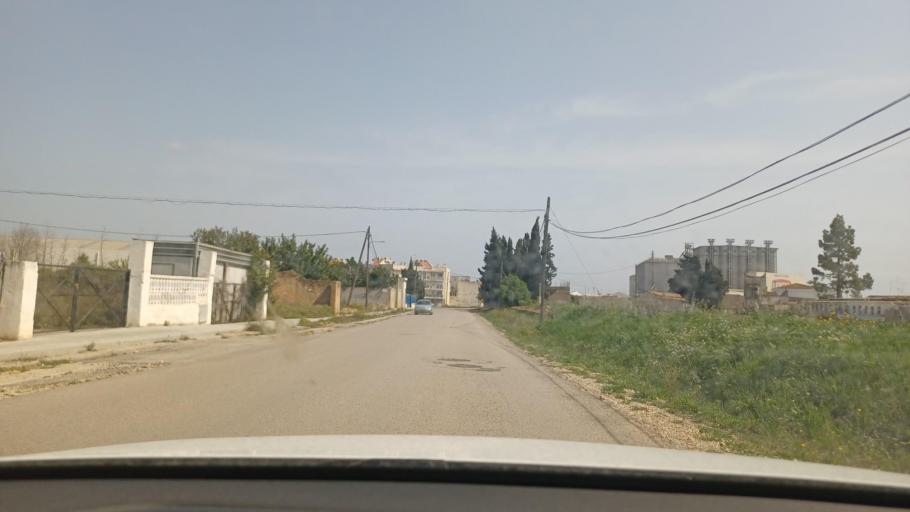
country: ES
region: Catalonia
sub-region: Provincia de Tarragona
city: Amposta
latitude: 40.7009
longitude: 0.5726
